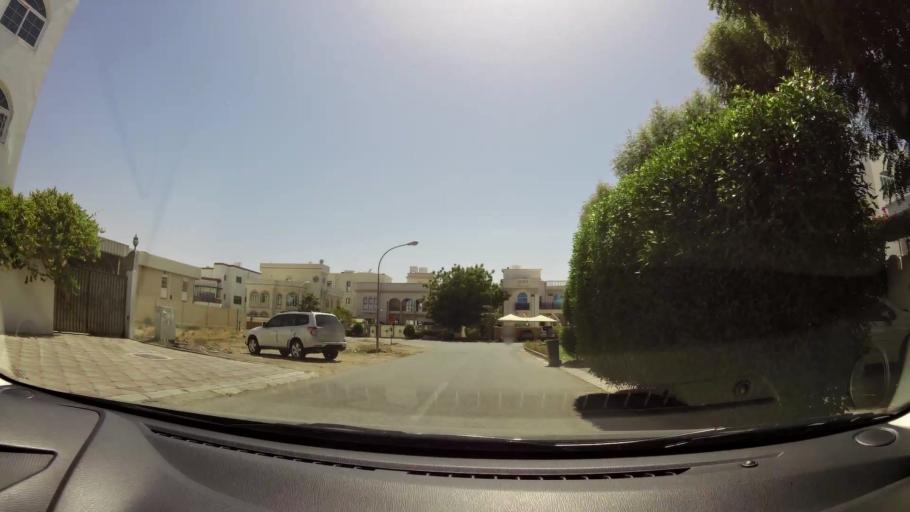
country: OM
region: Muhafazat Masqat
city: Bawshar
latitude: 23.5990
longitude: 58.3559
